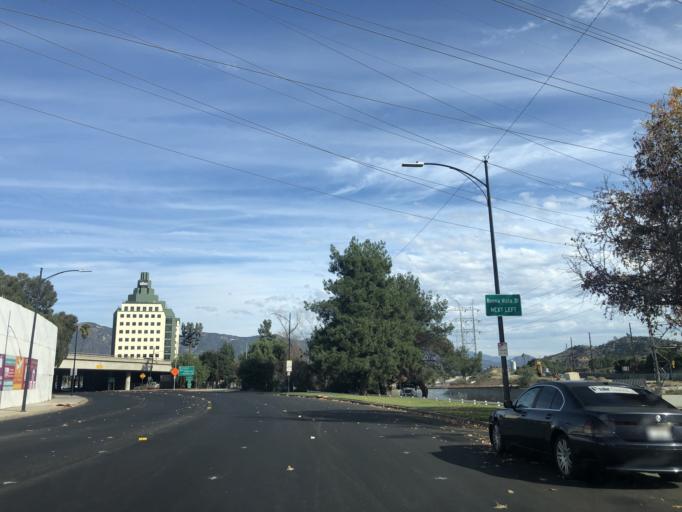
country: US
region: California
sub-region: Los Angeles County
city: Universal City
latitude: 34.1526
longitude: -118.3274
